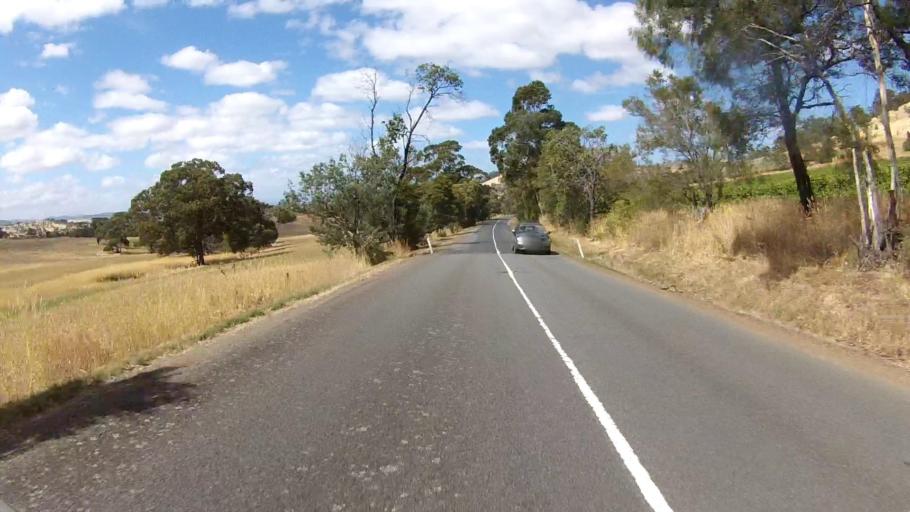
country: AU
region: Tasmania
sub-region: Sorell
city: Sorell
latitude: -42.7398
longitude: 147.4833
